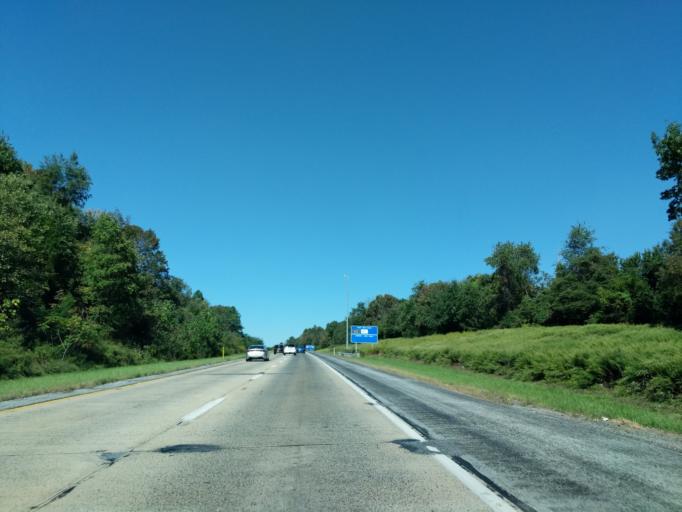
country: US
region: Pennsylvania
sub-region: Montgomery County
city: Audubon
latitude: 40.1490
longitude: -75.4585
